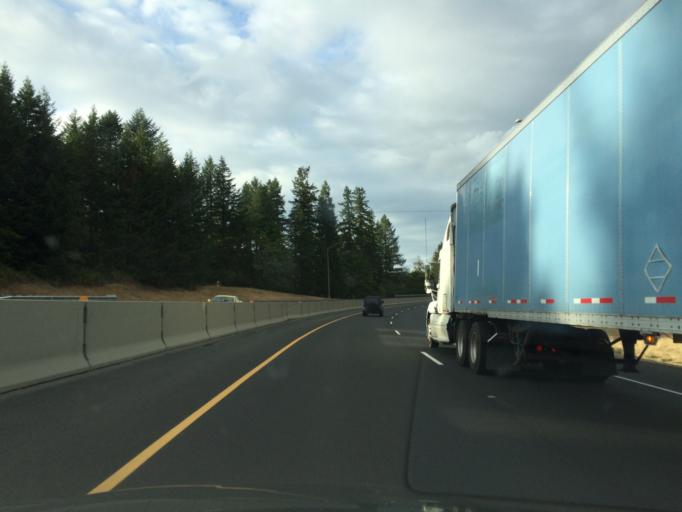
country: US
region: Oregon
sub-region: Douglas County
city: Drain
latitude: 43.7099
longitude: -123.2182
